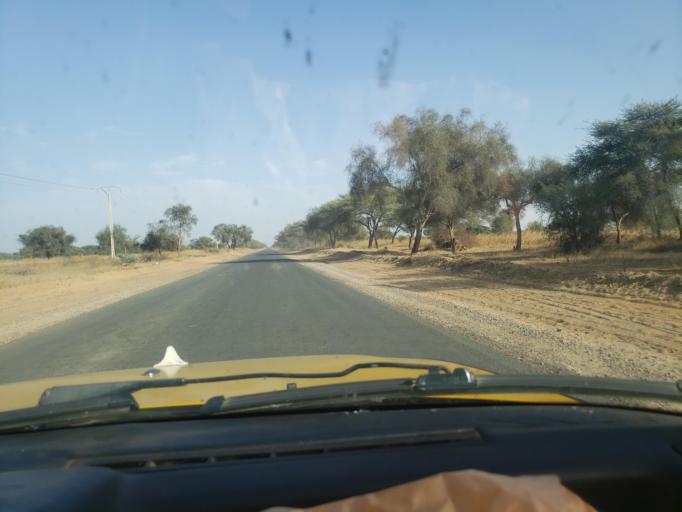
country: SN
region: Louga
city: Louga
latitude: 15.5057
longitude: -15.9609
